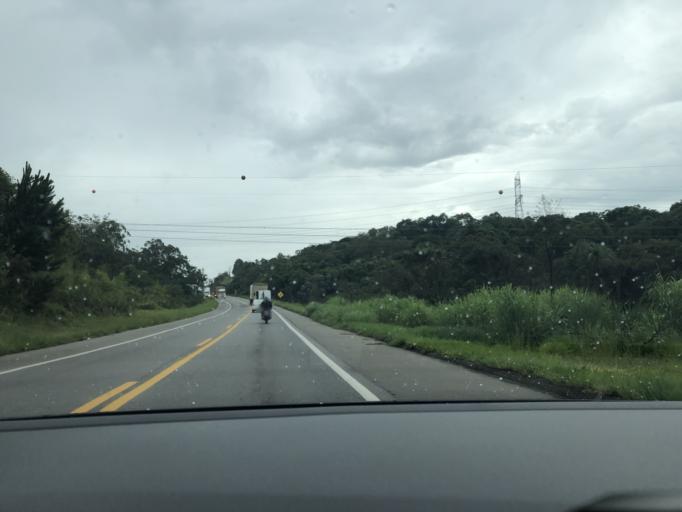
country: BR
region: Sao Paulo
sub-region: Jarinu
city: Jarinu
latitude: -23.1371
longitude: -46.7405
